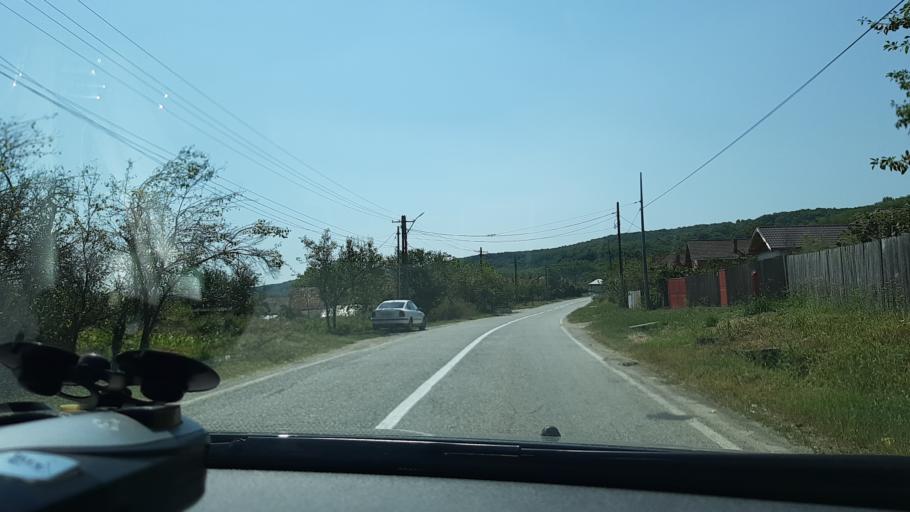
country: RO
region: Gorj
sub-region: Comuna Hurezani
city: Hurezani
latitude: 44.8420
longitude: 23.6397
